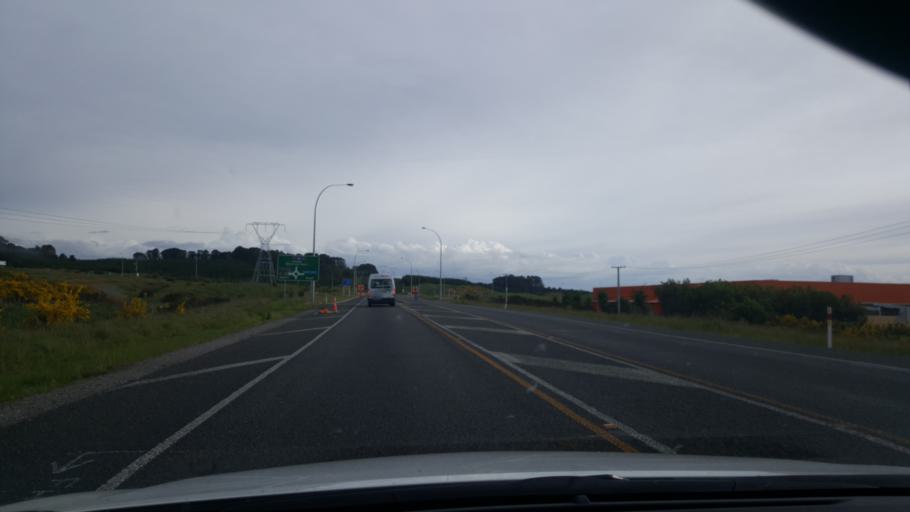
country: NZ
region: Waikato
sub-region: Taupo District
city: Taupo
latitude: -38.7016
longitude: 176.1118
